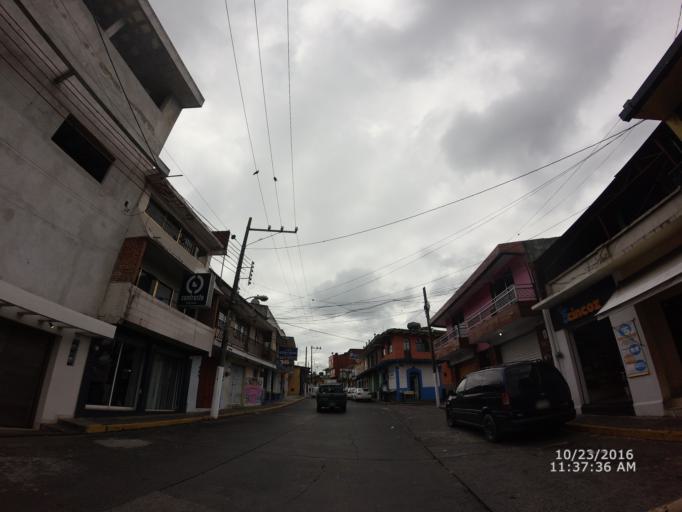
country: MX
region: Veracruz
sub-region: Xalapa
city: Xalapa de Enriquez
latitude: 19.5346
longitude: -96.9283
